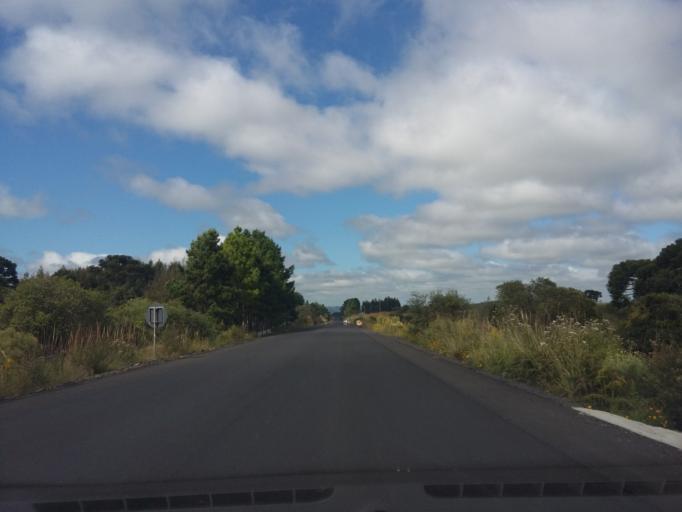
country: BR
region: Santa Catarina
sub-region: Sao Joaquim
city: Sao Joaquim
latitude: -28.0447
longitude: -50.0727
